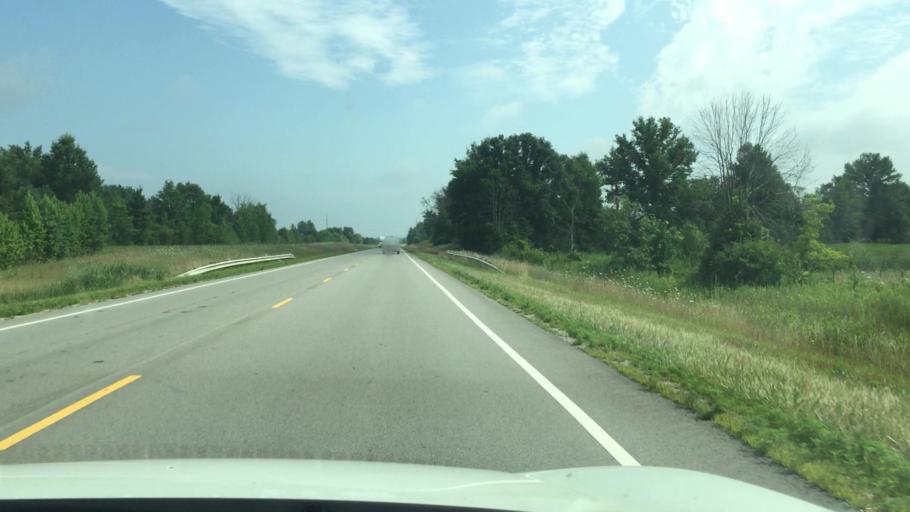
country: US
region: Ohio
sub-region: Union County
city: Marysville
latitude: 40.2194
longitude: -83.3975
